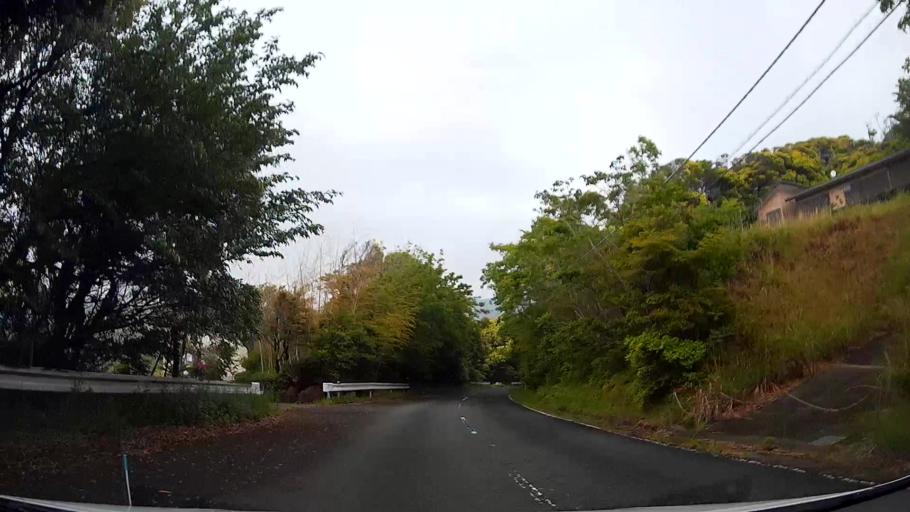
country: JP
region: Shizuoka
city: Shimoda
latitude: 34.6887
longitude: 138.7725
